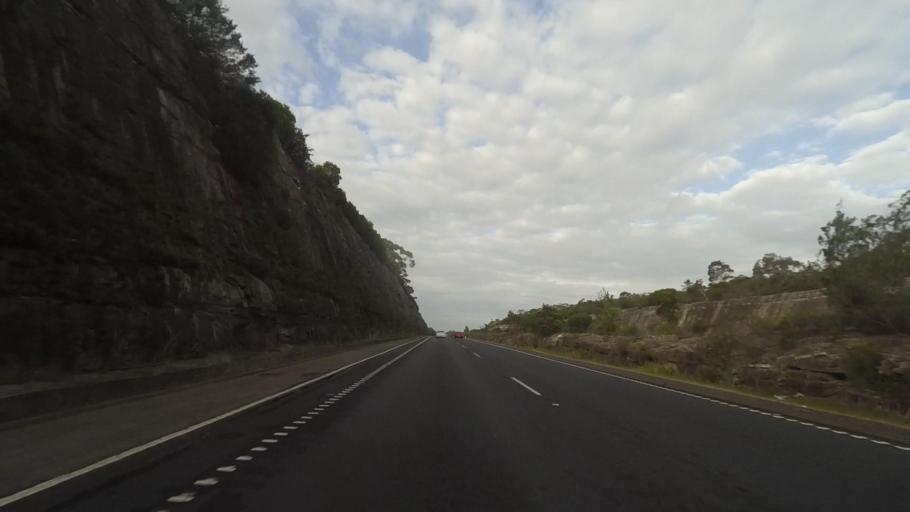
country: AU
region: New South Wales
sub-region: Wollongong
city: Helensburgh
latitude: -34.2229
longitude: 150.9514
